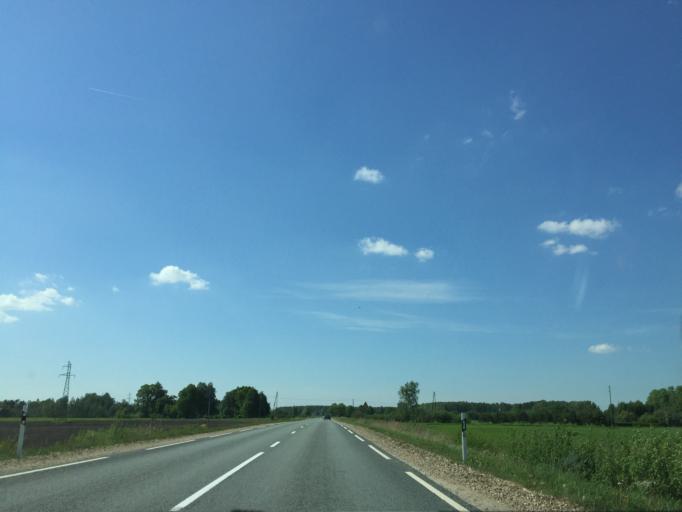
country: LV
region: Ozolnieku
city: Ozolnieki
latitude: 56.6254
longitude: 23.9022
